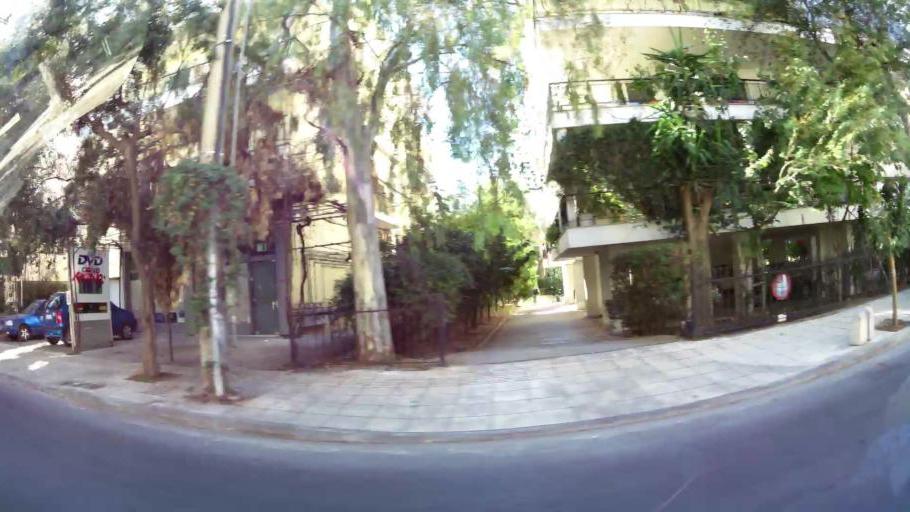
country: GR
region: Attica
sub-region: Nomarchia Athinas
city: Khalandrion
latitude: 38.0353
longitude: 23.8121
